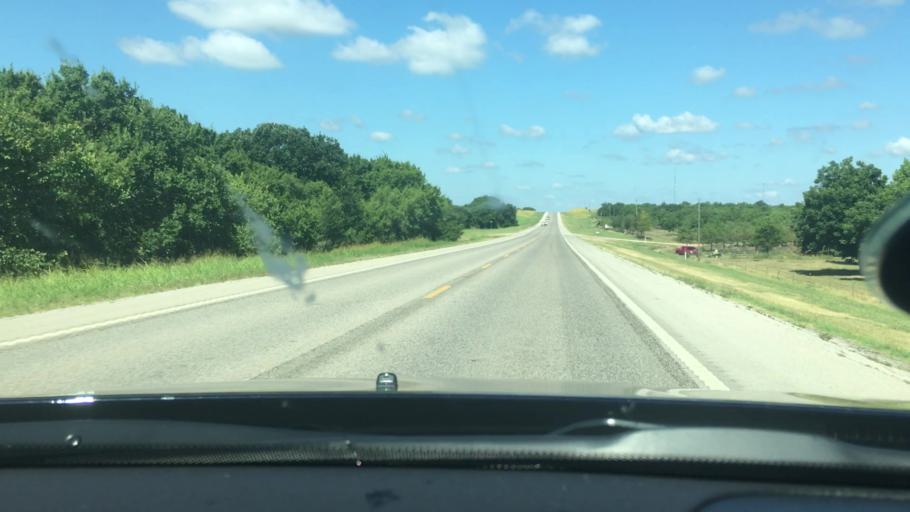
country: US
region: Oklahoma
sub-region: Marshall County
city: Oakland
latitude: 34.0999
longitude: -96.8612
